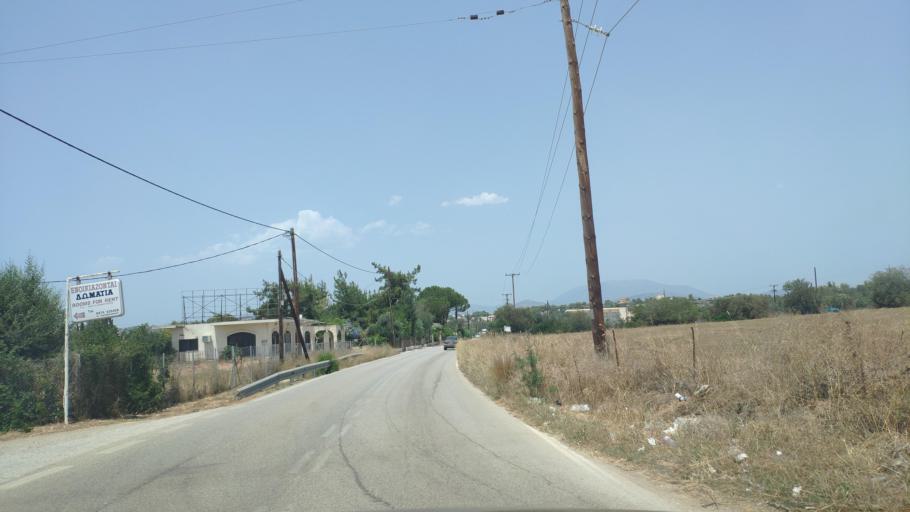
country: GR
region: Peloponnese
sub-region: Nomos Argolidos
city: Porto Cheli
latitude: 37.3121
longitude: 23.1581
